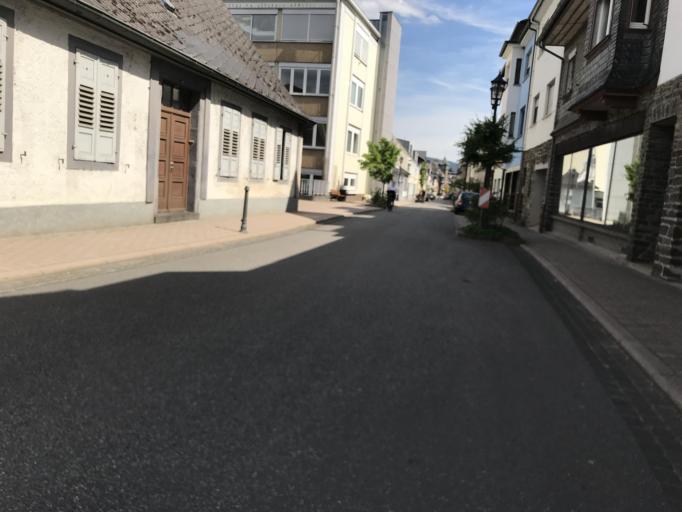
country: DE
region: Rheinland-Pfalz
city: Oberwesel
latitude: 50.1101
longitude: 7.7224
